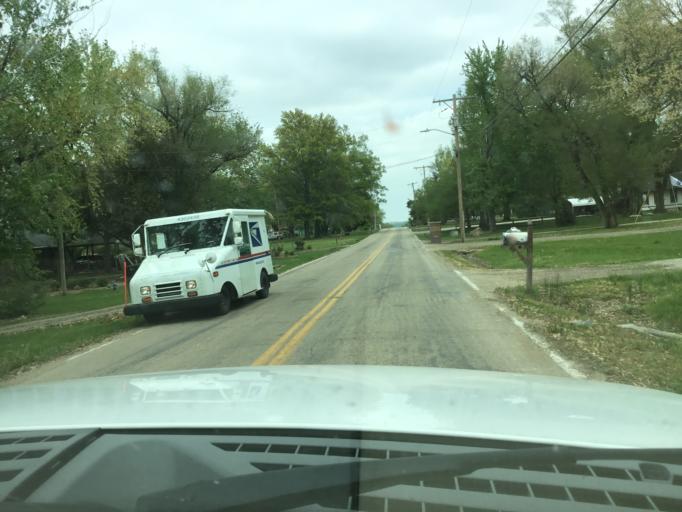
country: US
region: Kansas
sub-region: Shawnee County
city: Topeka
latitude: 39.0471
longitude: -95.6227
